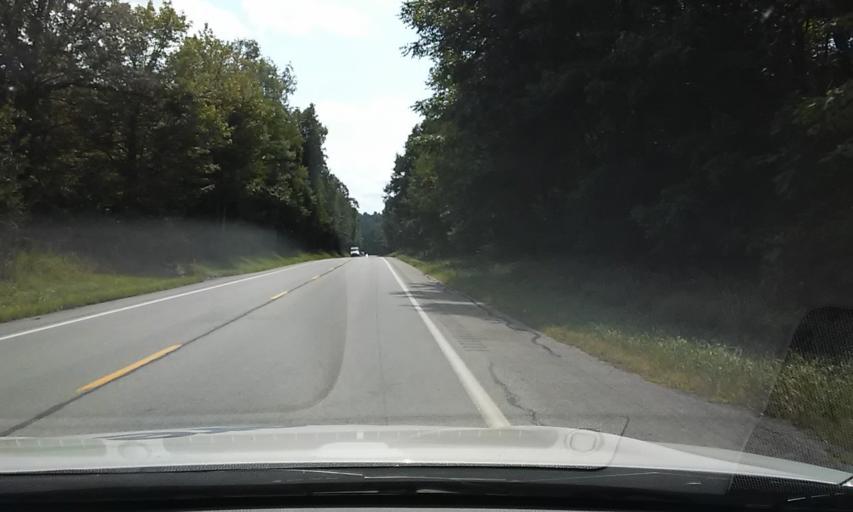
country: US
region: Pennsylvania
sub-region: Indiana County
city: Clymer
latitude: 40.7782
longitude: -79.0551
